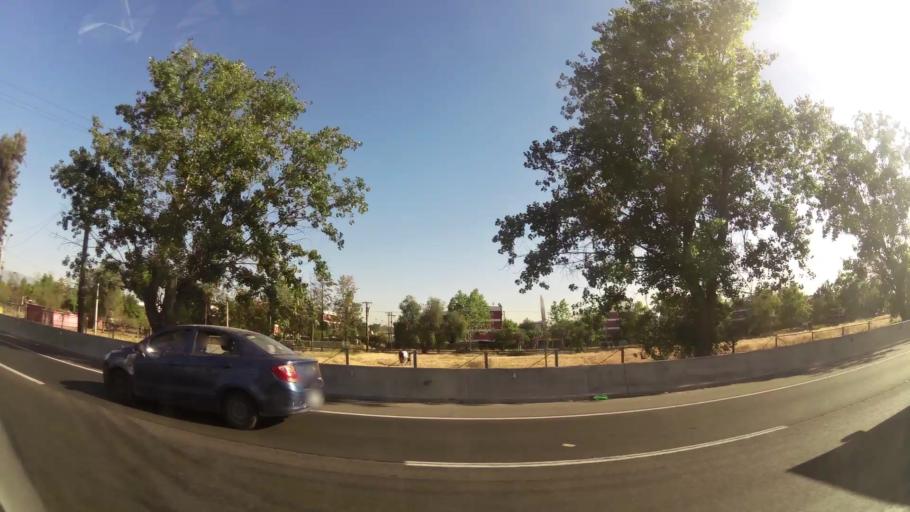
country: CL
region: Santiago Metropolitan
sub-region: Provincia de Santiago
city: Lo Prado
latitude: -33.4514
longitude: -70.7496
